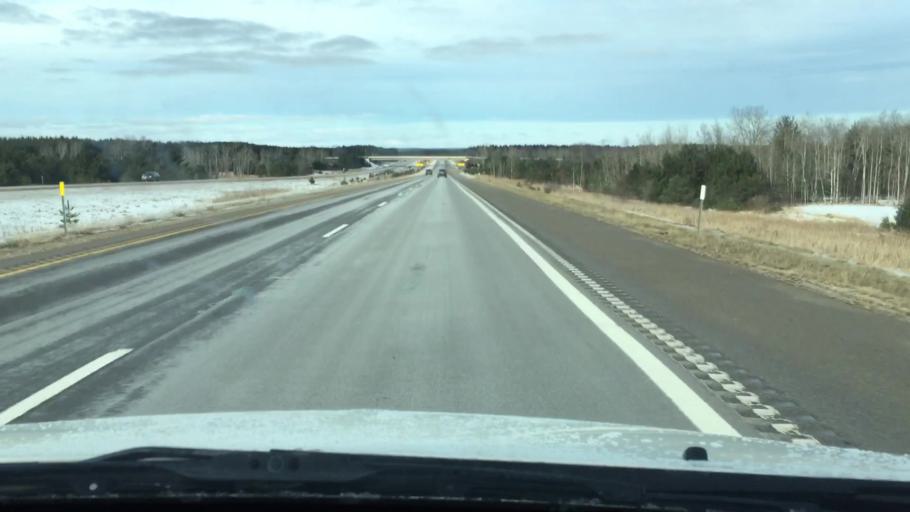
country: US
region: Michigan
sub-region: Wexford County
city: Manton
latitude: 44.4465
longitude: -85.3949
